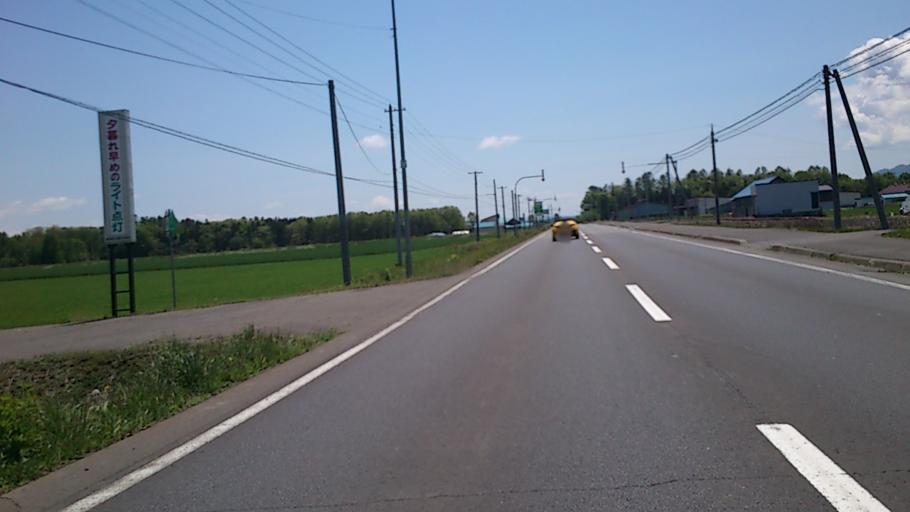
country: JP
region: Hokkaido
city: Nayoro
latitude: 44.5154
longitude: 142.3303
